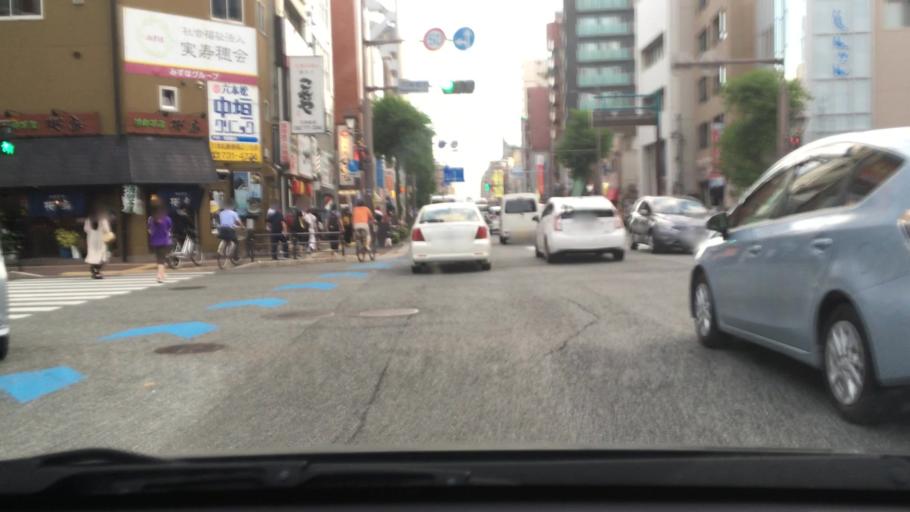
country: JP
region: Fukuoka
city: Fukuoka-shi
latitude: 33.5771
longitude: 130.3762
